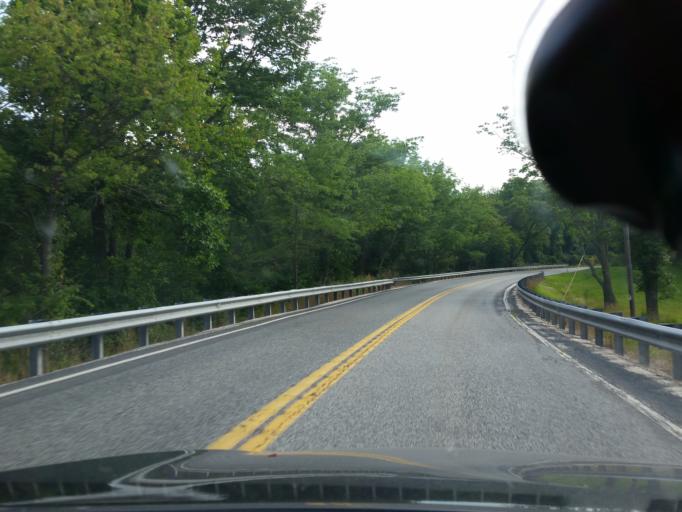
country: US
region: Pennsylvania
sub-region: Perry County
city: Duncannon
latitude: 40.3240
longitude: -77.0683
